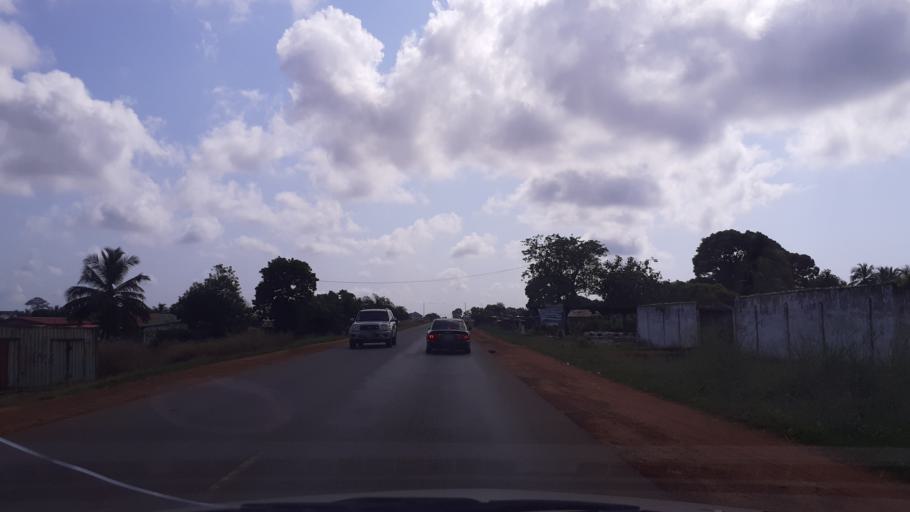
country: LR
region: Montserrado
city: Monrovia
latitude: 6.2252
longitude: -10.6149
